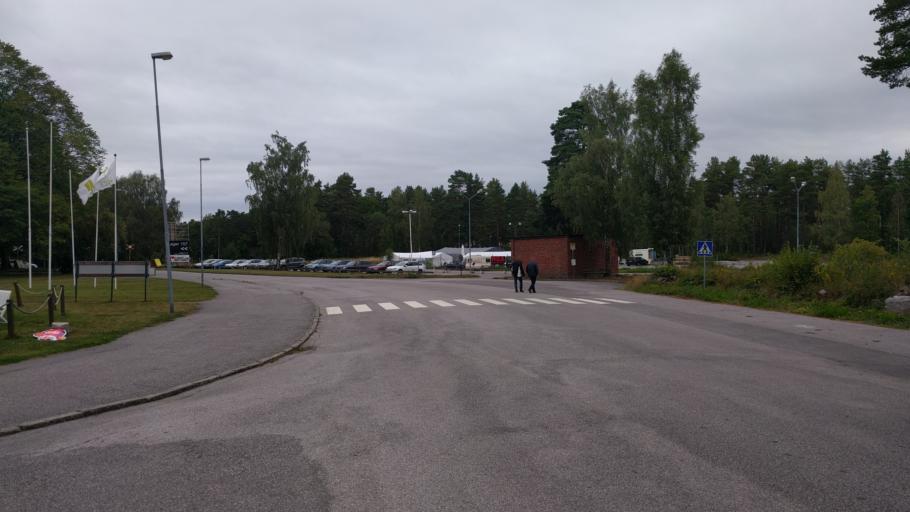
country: SE
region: Kalmar
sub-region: Vasterviks Kommun
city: Vaestervik
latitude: 57.7431
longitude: 16.6618
